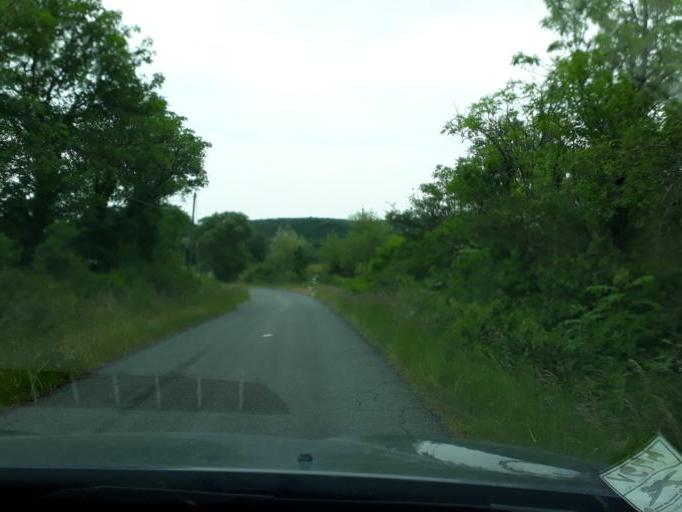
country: FR
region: Languedoc-Roussillon
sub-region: Departement de l'Herault
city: Lodeve
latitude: 43.8403
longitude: 3.2752
